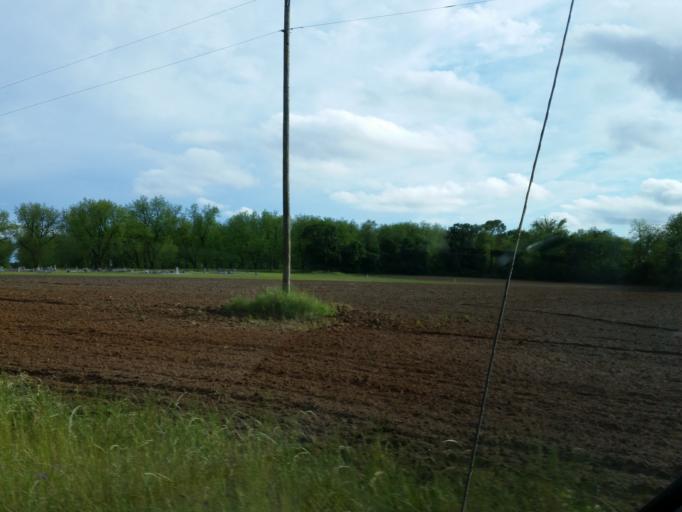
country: US
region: Georgia
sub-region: Dooly County
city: Vienna
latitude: 32.1633
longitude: -83.7623
